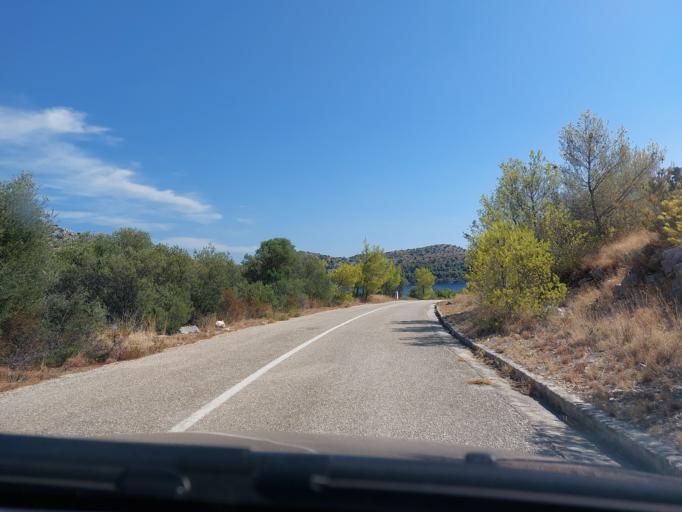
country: HR
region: Dubrovacko-Neretvanska
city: Smokvica
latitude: 42.7395
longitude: 16.8852
